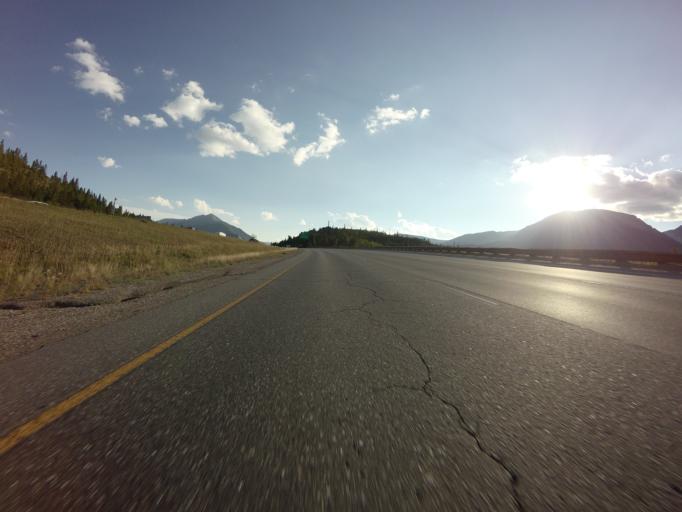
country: US
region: Colorado
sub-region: Summit County
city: Silverthorne
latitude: 39.6100
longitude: -106.0791
